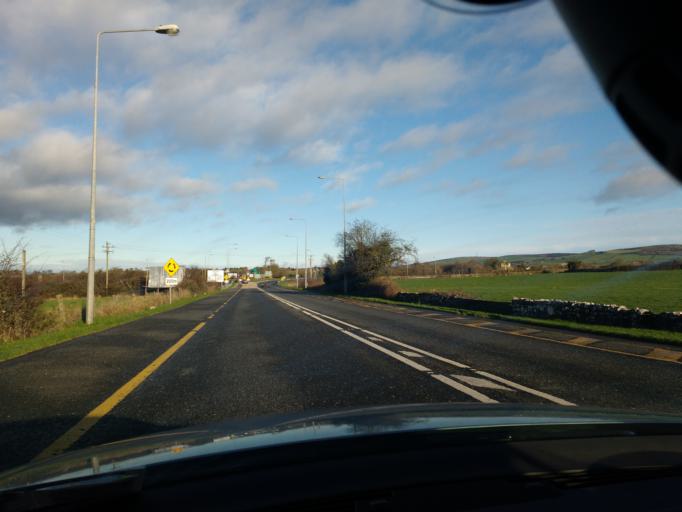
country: IE
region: Leinster
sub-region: Laois
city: Rathdowney
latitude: 52.7256
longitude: -7.5747
